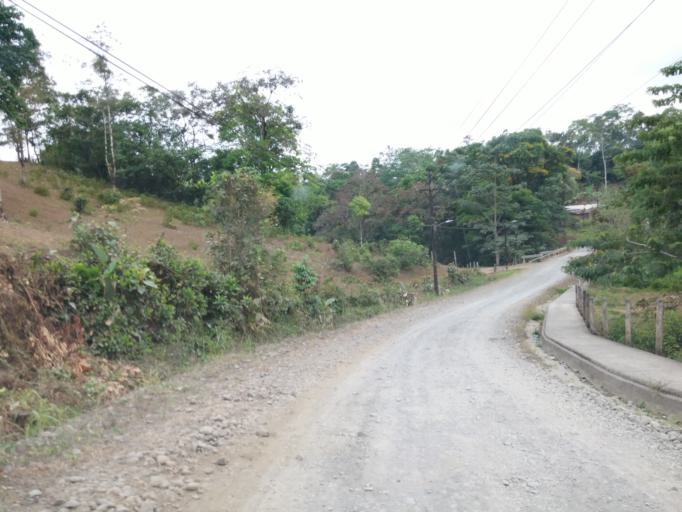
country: CR
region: Alajuela
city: Quesada
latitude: 10.3208
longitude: -84.5159
